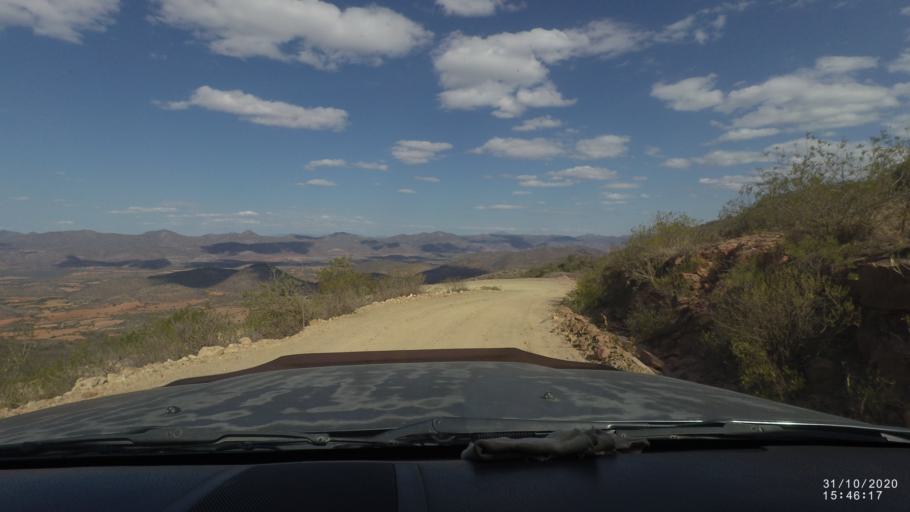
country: BO
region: Chuquisaca
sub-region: Provincia Zudanez
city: Mojocoya
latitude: -18.3160
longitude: -64.7167
